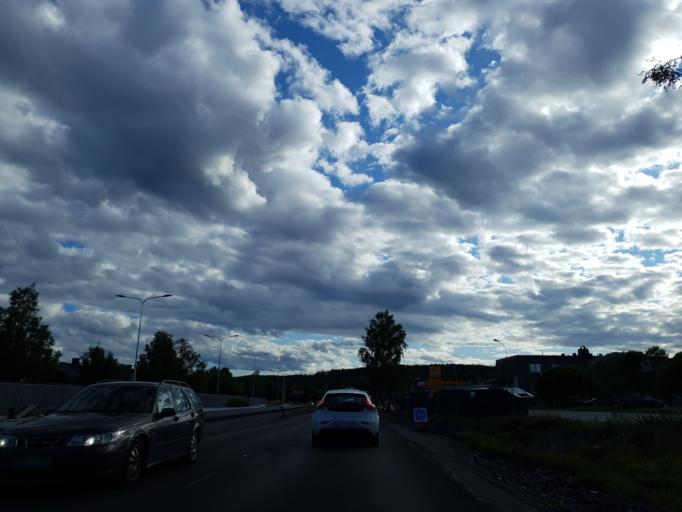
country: SE
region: Vaesternorrland
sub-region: Haernoesands Kommun
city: Haernoesand
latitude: 62.6768
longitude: 17.8429
